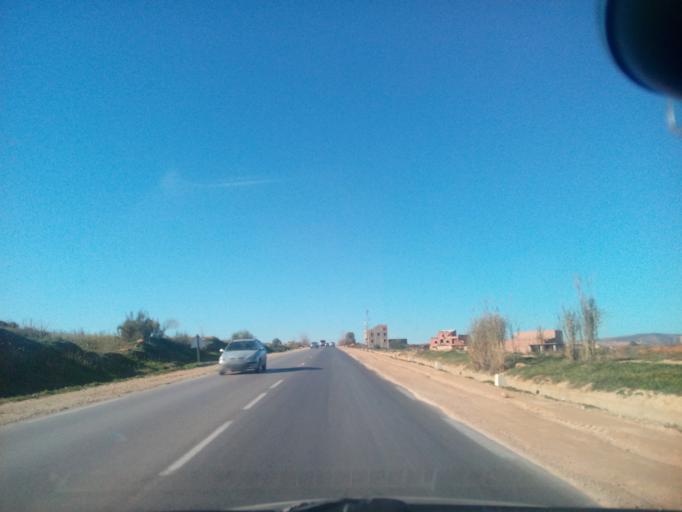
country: DZ
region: Relizane
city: Relizane
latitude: 35.9070
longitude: 0.5104
